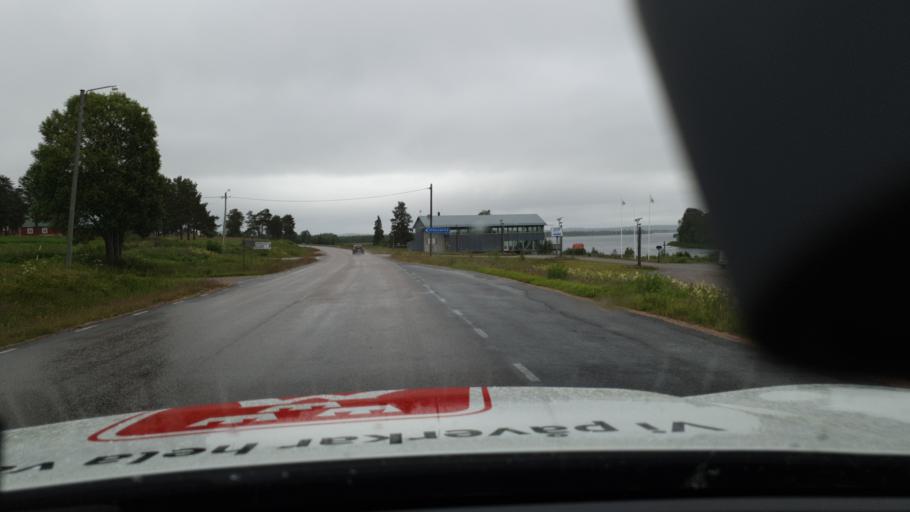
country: SE
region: Norrbotten
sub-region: Overtornea Kommun
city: OEvertornea
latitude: 66.5318
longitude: 23.7803
